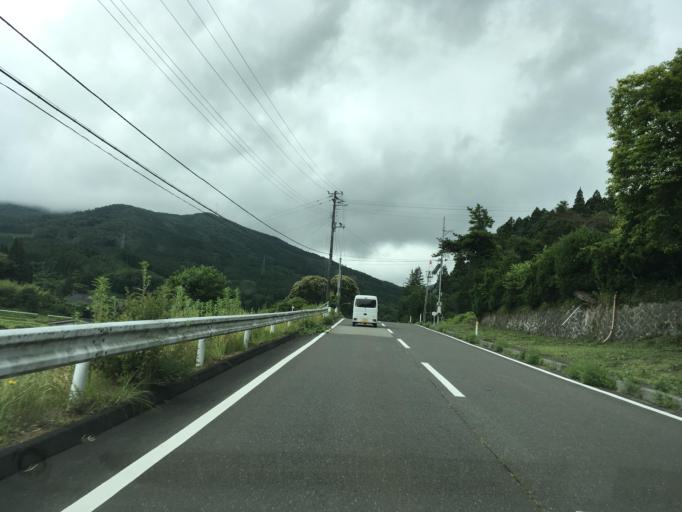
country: JP
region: Iwate
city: Ofunato
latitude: 38.8931
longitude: 141.4839
